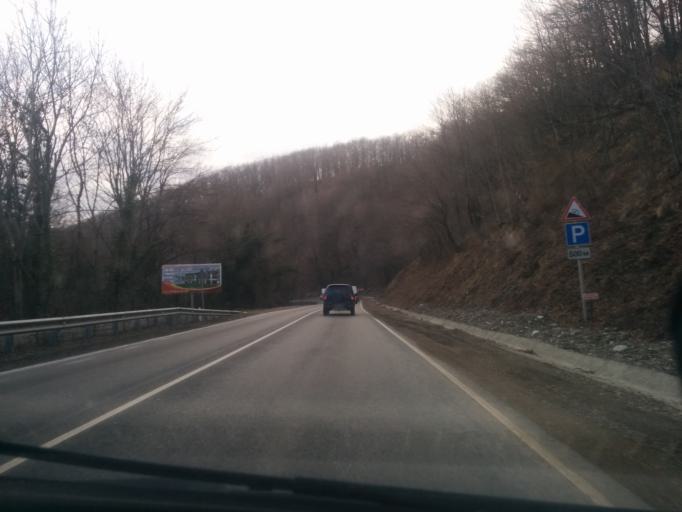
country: RU
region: Krasnodarskiy
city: Agoy
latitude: 44.1315
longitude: 39.0470
